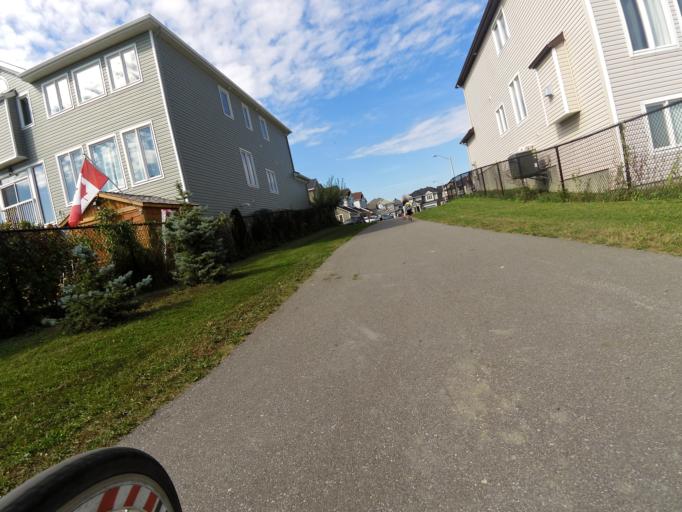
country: CA
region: Ontario
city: Bells Corners
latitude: 45.2715
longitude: -75.7776
